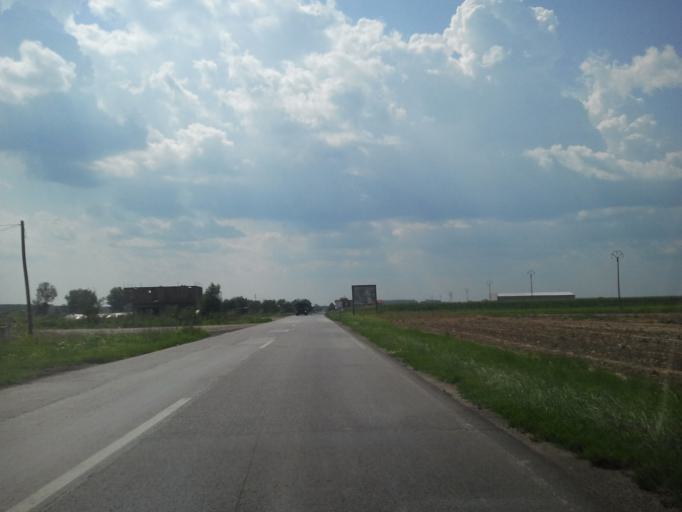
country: RS
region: Autonomna Pokrajina Vojvodina
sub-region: Juznobacki Okrug
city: Beocin
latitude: 45.2401
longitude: 19.6749
